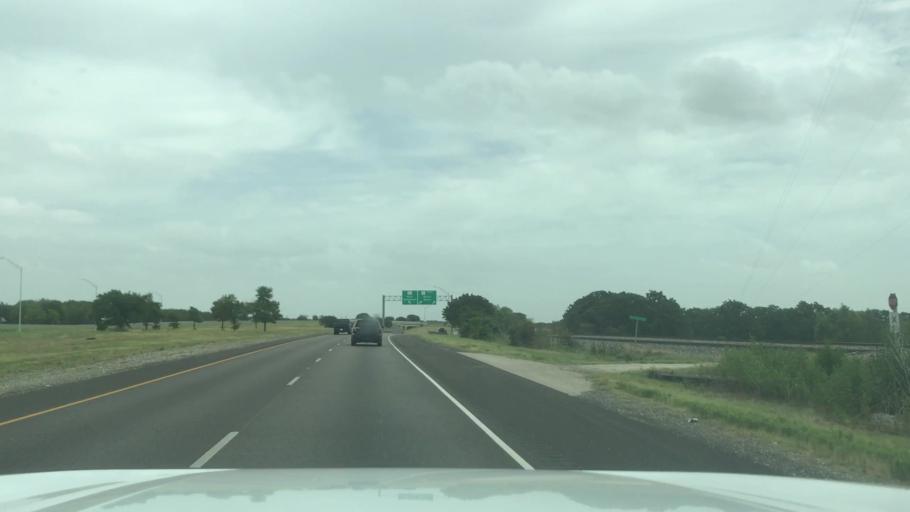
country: US
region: Texas
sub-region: McLennan County
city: Riesel
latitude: 31.5170
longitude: -96.9632
